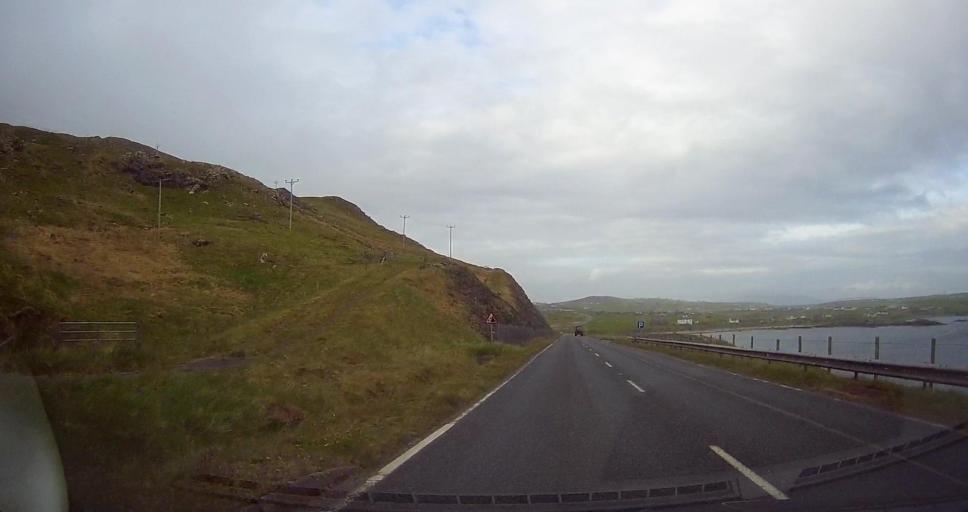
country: GB
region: Scotland
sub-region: Shetland Islands
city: Sandwick
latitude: 60.0285
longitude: -1.2368
